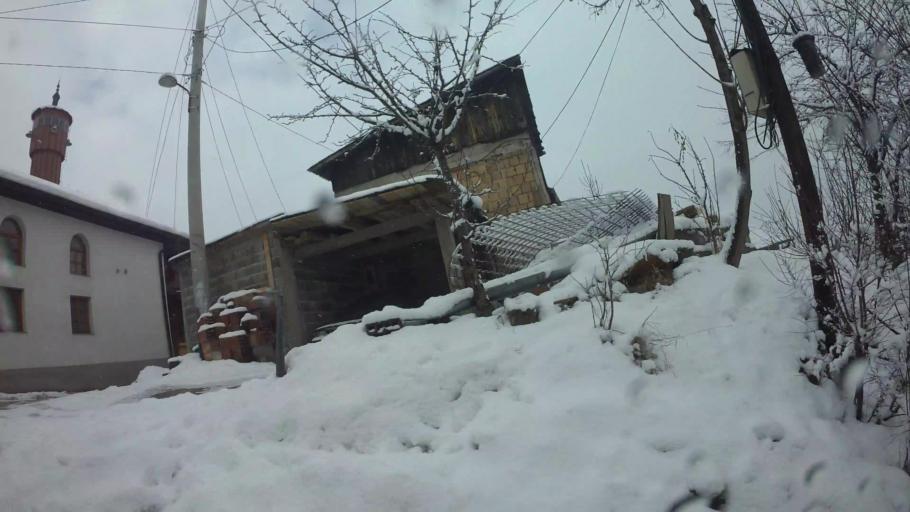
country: BA
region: Federation of Bosnia and Herzegovina
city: Kobilja Glava
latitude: 43.8489
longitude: 18.4255
